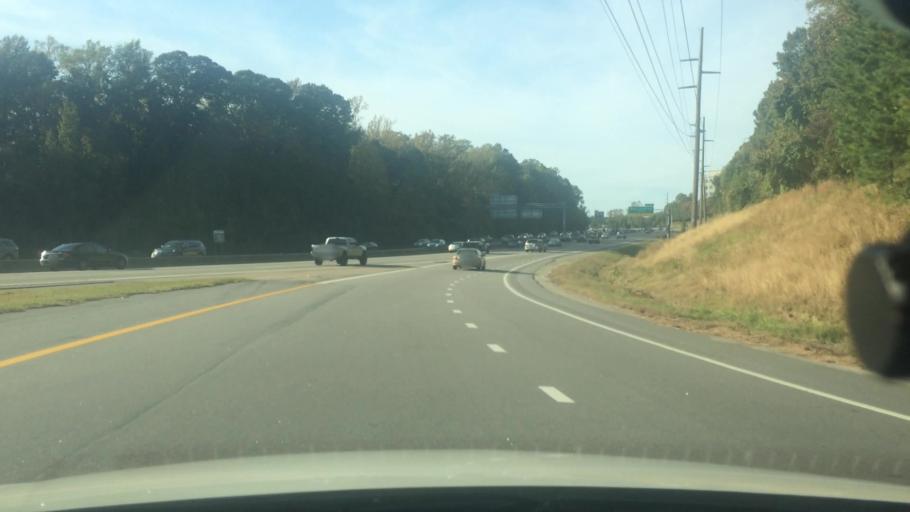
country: US
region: North Carolina
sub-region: Wake County
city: Raleigh
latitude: 35.8164
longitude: -78.6062
